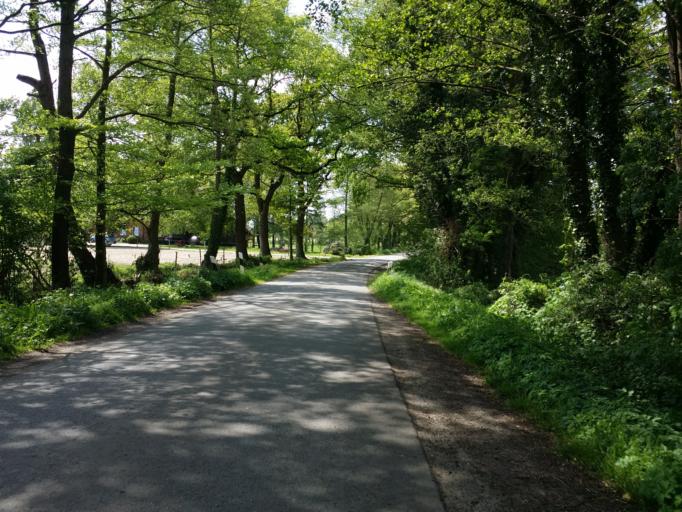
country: DE
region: Lower Saxony
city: Axstedt
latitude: 53.3029
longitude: 8.7519
